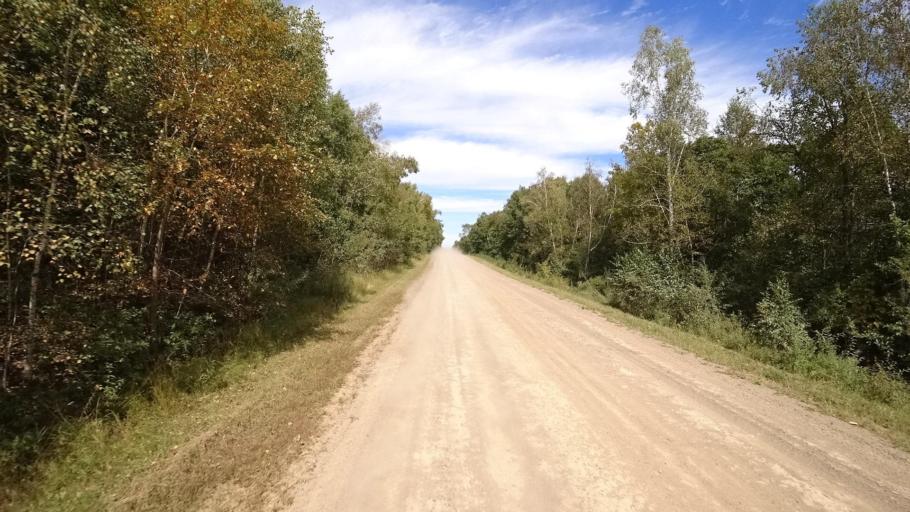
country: RU
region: Primorskiy
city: Yakovlevka
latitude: 44.6692
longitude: 133.6109
